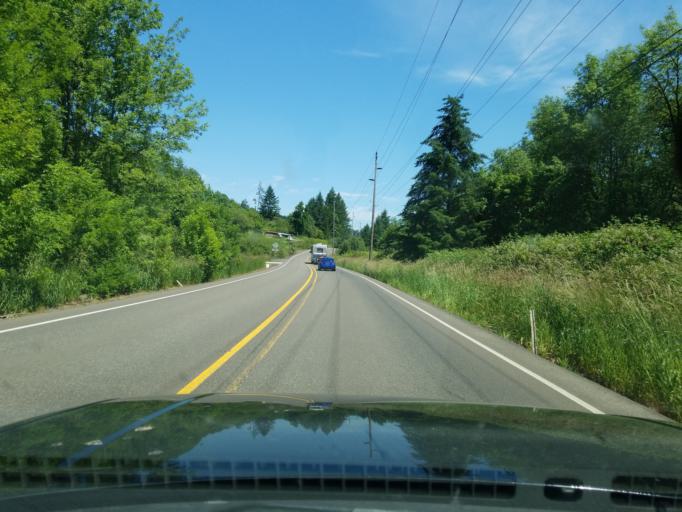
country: US
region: Oregon
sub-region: Yamhill County
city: Yamhill
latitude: 45.3854
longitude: -123.1393
